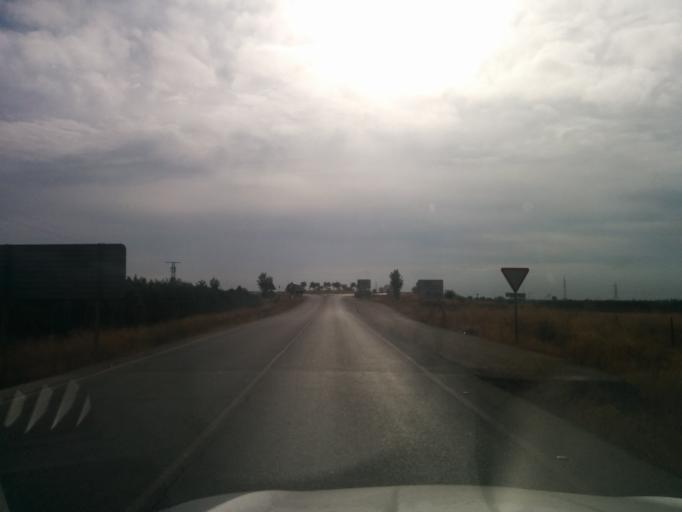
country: ES
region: Andalusia
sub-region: Provincia de Sevilla
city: La Rinconada
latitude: 37.4547
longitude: -5.9742
